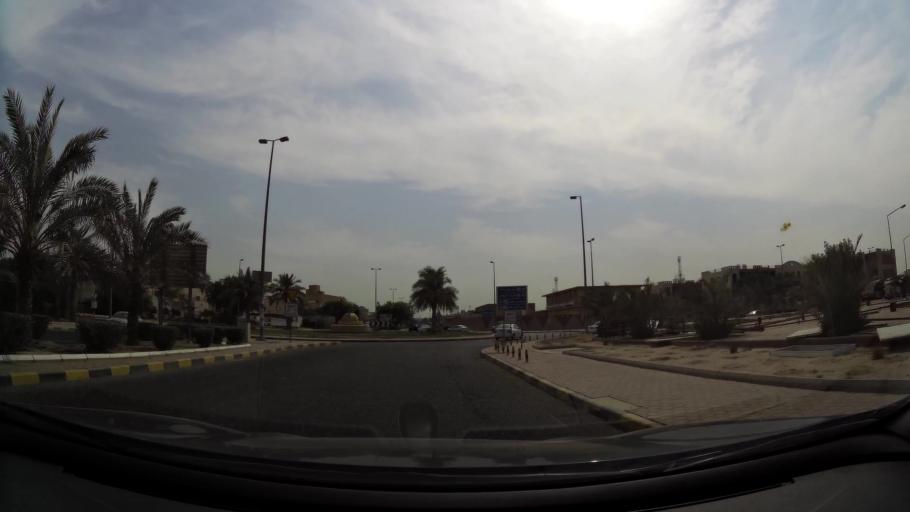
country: KW
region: Al Asimah
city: Ash Shamiyah
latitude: 29.3417
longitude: 47.9801
